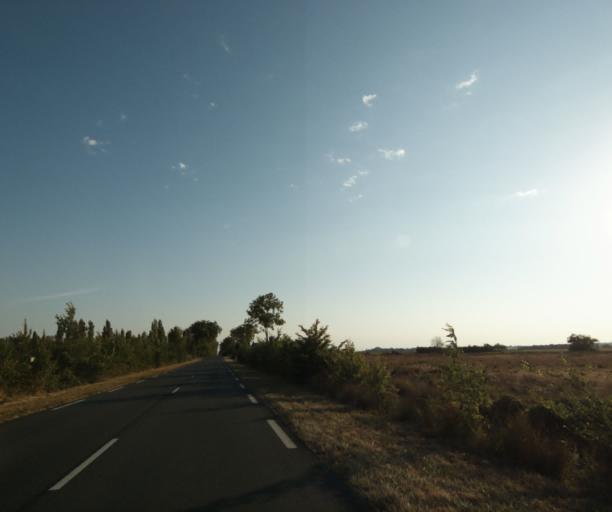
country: FR
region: Poitou-Charentes
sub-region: Departement de la Charente-Maritime
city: Tonnay-Charente
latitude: 45.9633
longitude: -0.9268
